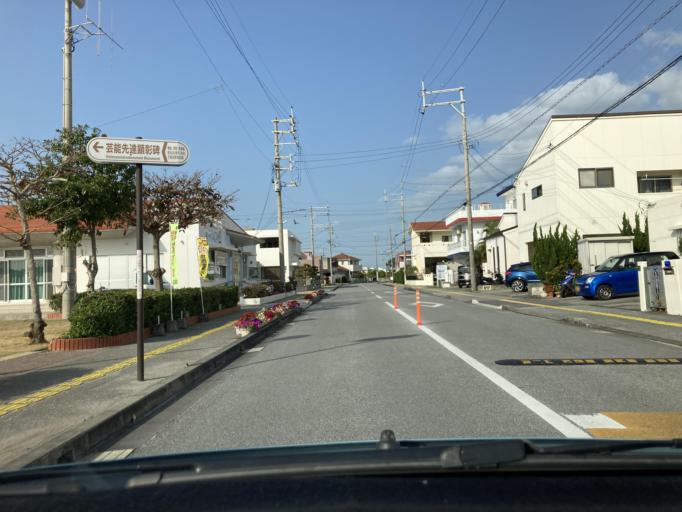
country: JP
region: Okinawa
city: Ginowan
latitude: 26.2082
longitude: 127.7607
